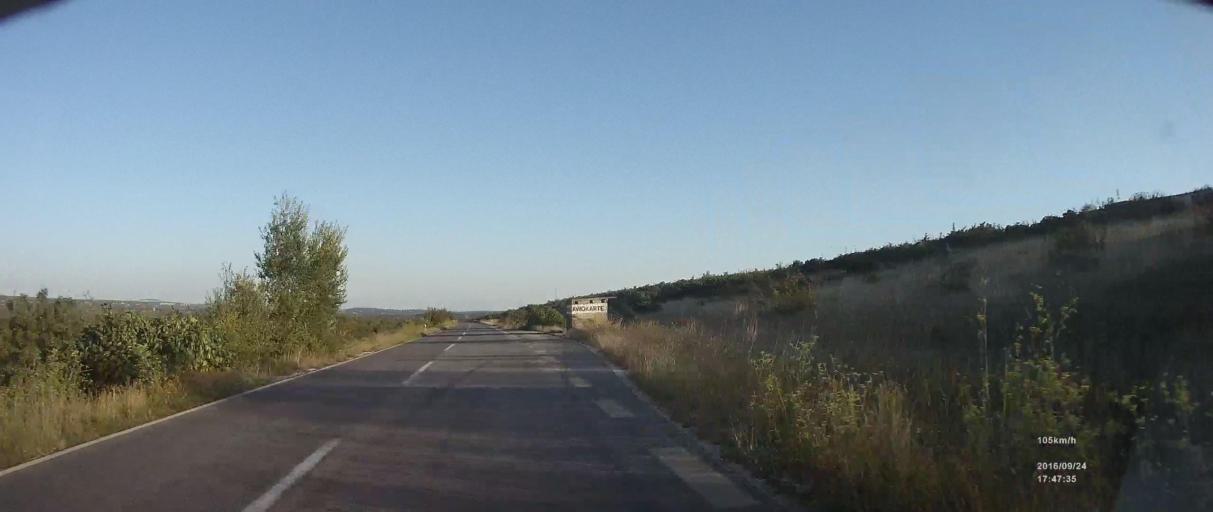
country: HR
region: Zadarska
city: Polaca
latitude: 44.0735
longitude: 15.5251
